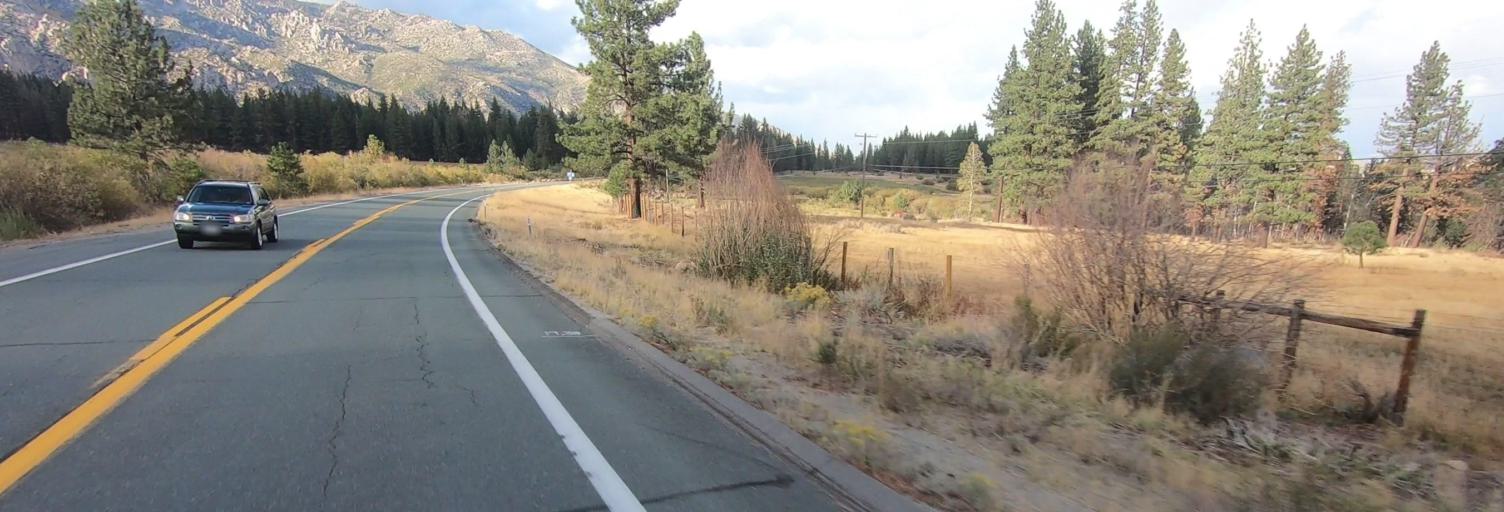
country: US
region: Nevada
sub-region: Douglas County
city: Gardnerville Ranchos
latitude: 38.7515
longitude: -119.8154
